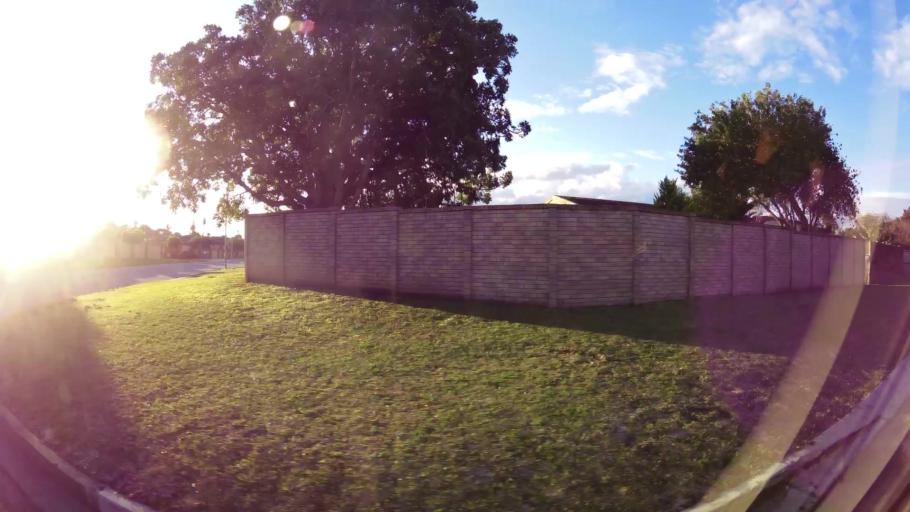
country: ZA
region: Eastern Cape
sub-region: Nelson Mandela Bay Metropolitan Municipality
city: Port Elizabeth
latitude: -33.9744
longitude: 25.4994
